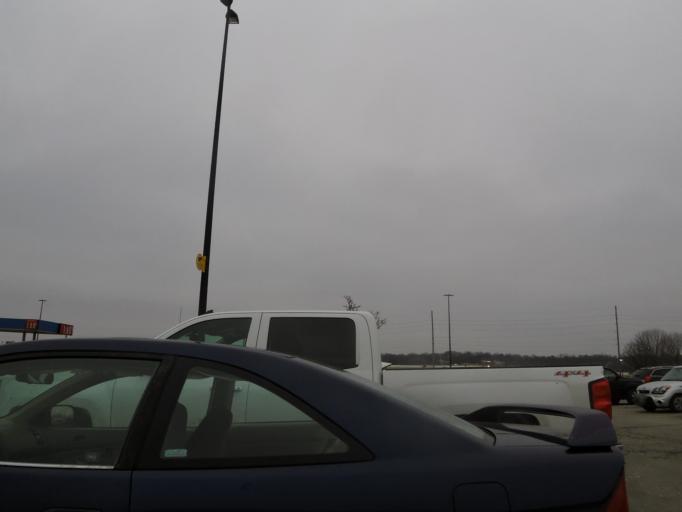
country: US
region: Missouri
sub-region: Marion County
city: Hannibal
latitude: 39.7243
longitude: -91.3987
